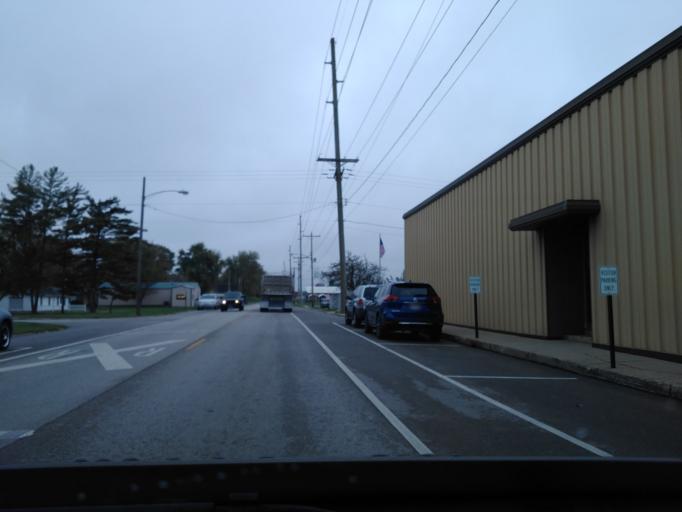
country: US
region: Illinois
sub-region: Bond County
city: Greenville
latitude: 38.8836
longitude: -89.4145
